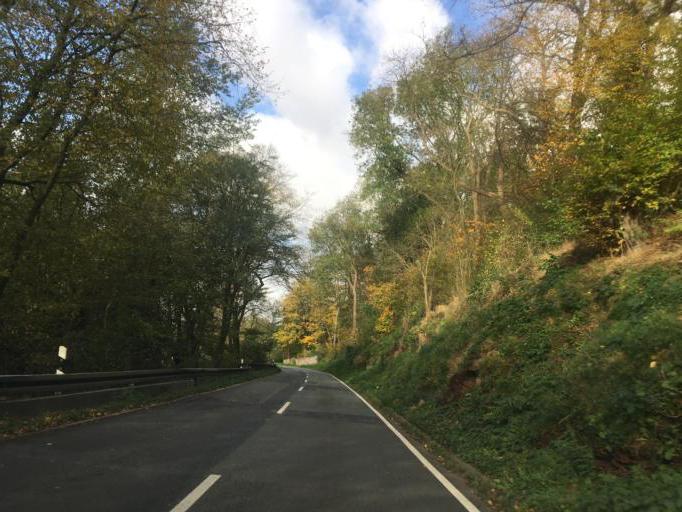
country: DE
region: Lower Saxony
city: Furstenberg
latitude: 51.7474
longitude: 9.4037
